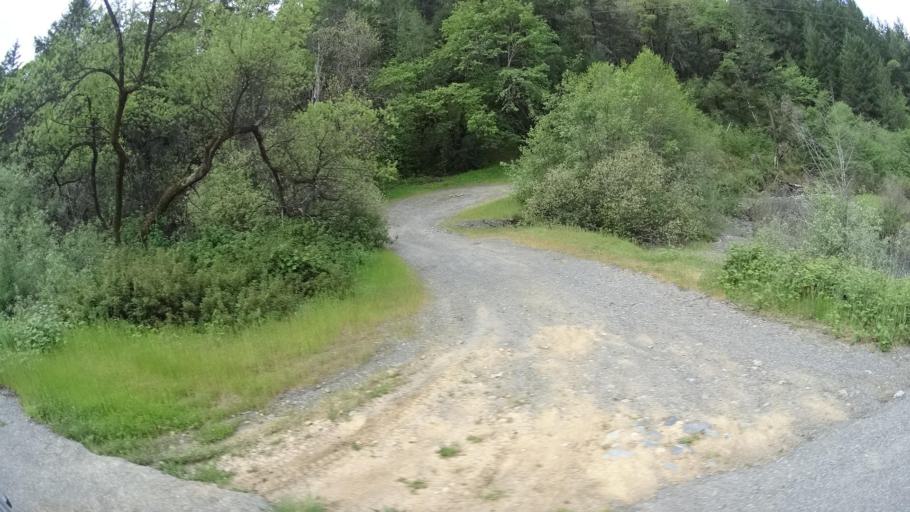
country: US
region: California
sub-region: Humboldt County
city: Redway
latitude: 40.1915
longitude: -123.5889
